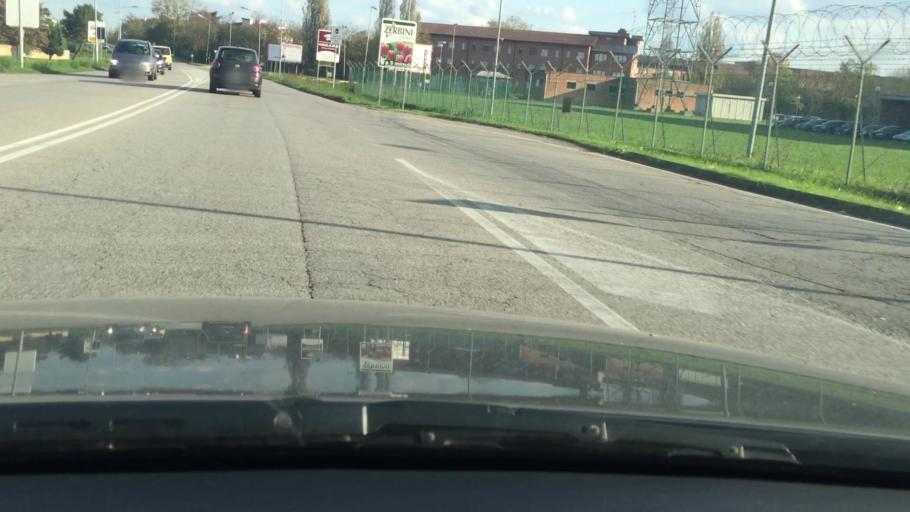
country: IT
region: Emilia-Romagna
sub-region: Provincia di Ferrara
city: Ferrara
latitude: 44.8167
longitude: 11.6096
